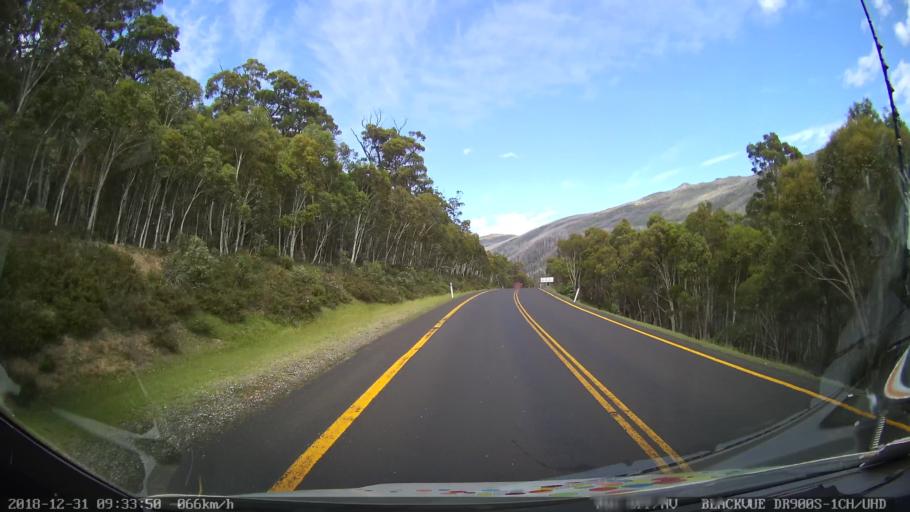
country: AU
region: New South Wales
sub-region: Snowy River
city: Jindabyne
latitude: -36.4503
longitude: 148.4185
